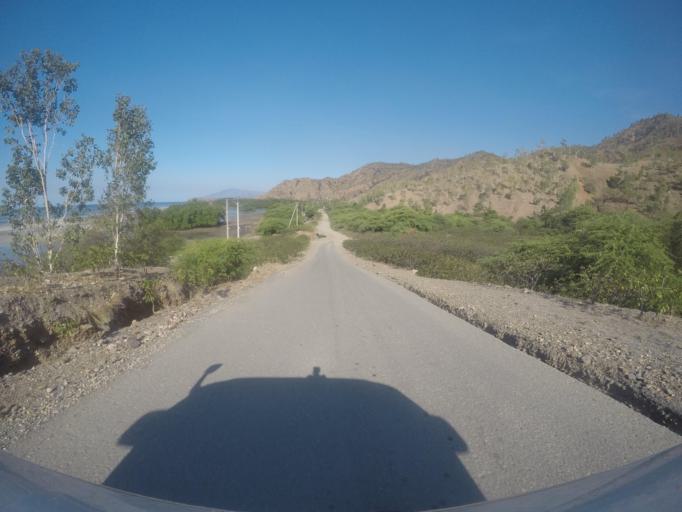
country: TL
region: Dili
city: Dili
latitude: -8.5276
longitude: 125.6312
